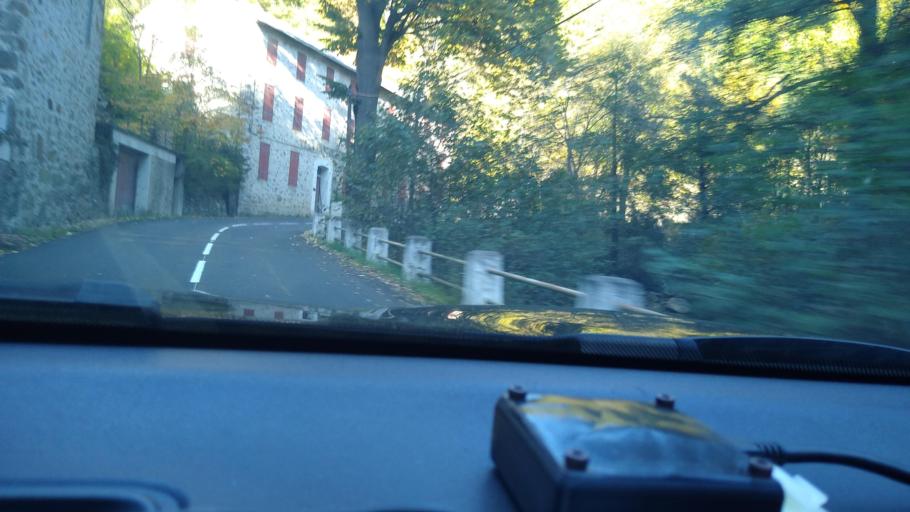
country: FR
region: Languedoc-Roussillon
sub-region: Departement de l'Aude
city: Quillan
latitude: 42.7192
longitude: 2.1243
